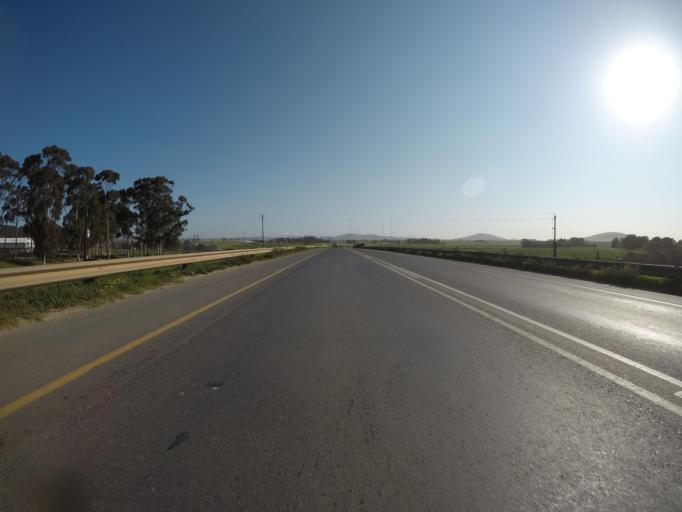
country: ZA
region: Western Cape
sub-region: City of Cape Town
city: Kraaifontein
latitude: -33.7821
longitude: 18.7132
